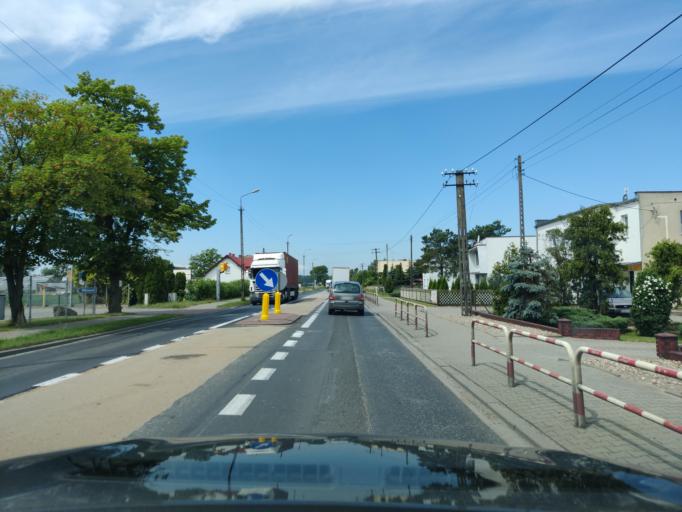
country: PL
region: Greater Poland Voivodeship
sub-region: Powiat grodziski
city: Granowo
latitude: 52.2228
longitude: 16.5213
